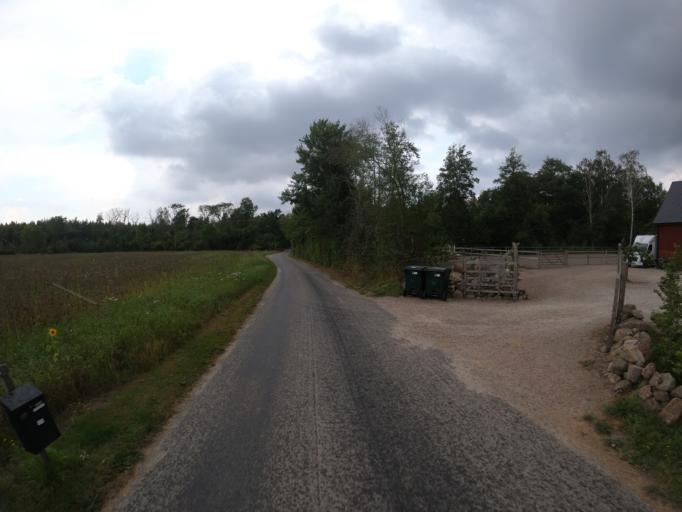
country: SE
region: Skane
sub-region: Lunds Kommun
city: Genarp
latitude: 55.6929
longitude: 13.3287
